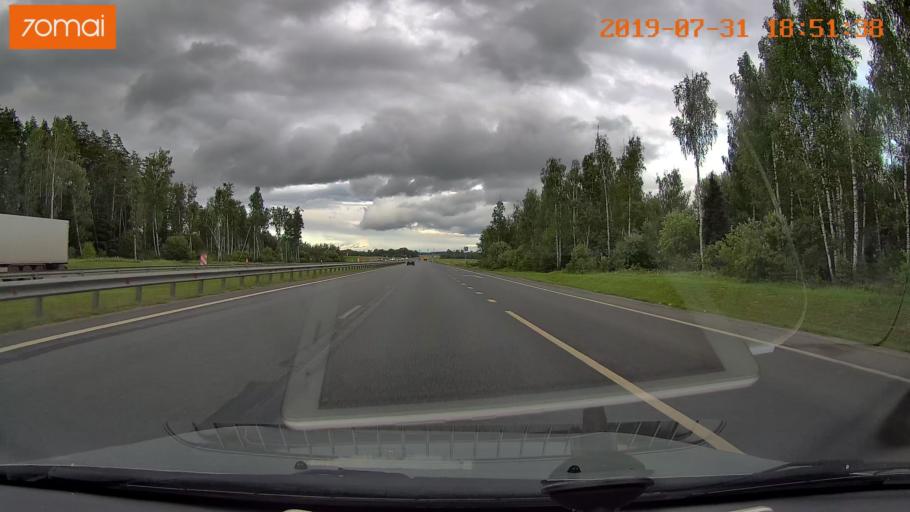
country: RU
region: Moskovskaya
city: Voskresensk
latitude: 55.2205
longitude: 38.6124
